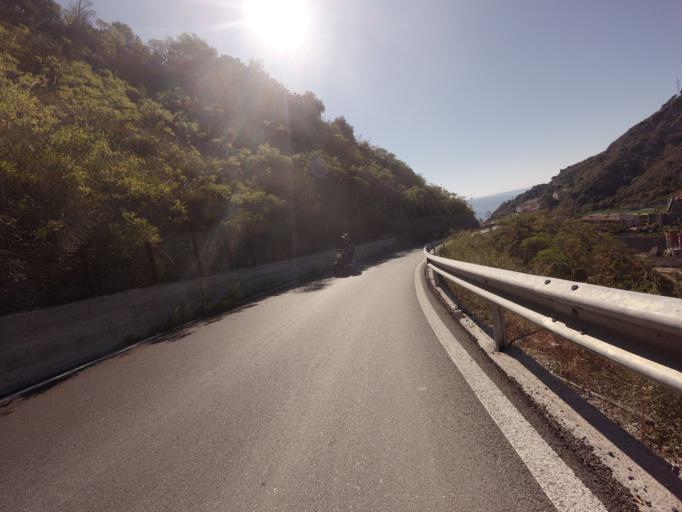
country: IT
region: Sicily
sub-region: Messina
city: Castelmola
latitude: 37.8479
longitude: 15.2776
